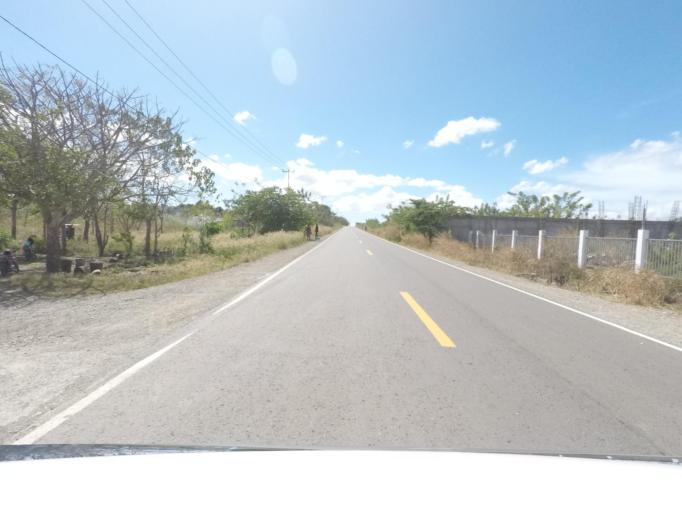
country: TL
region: Baucau
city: Baucau
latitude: -8.4885
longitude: 126.3729
